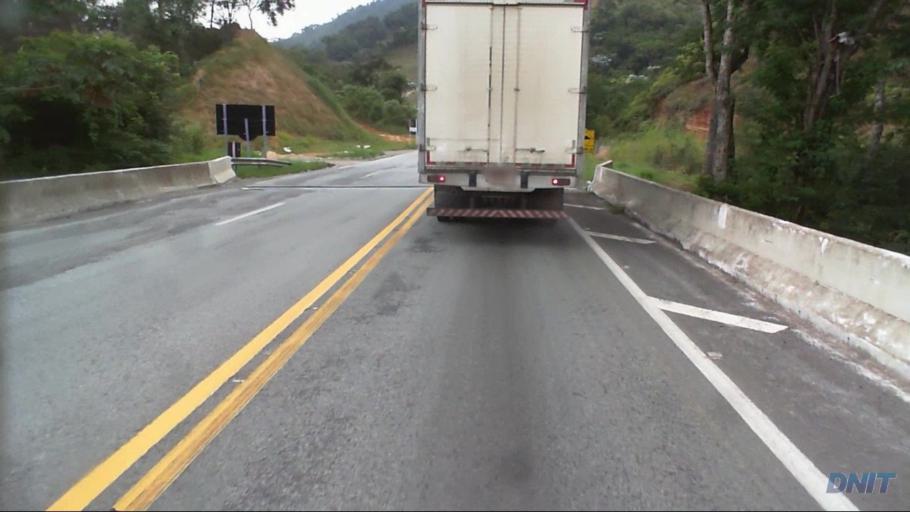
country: BR
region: Minas Gerais
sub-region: Nova Era
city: Nova Era
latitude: -19.6558
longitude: -42.9576
